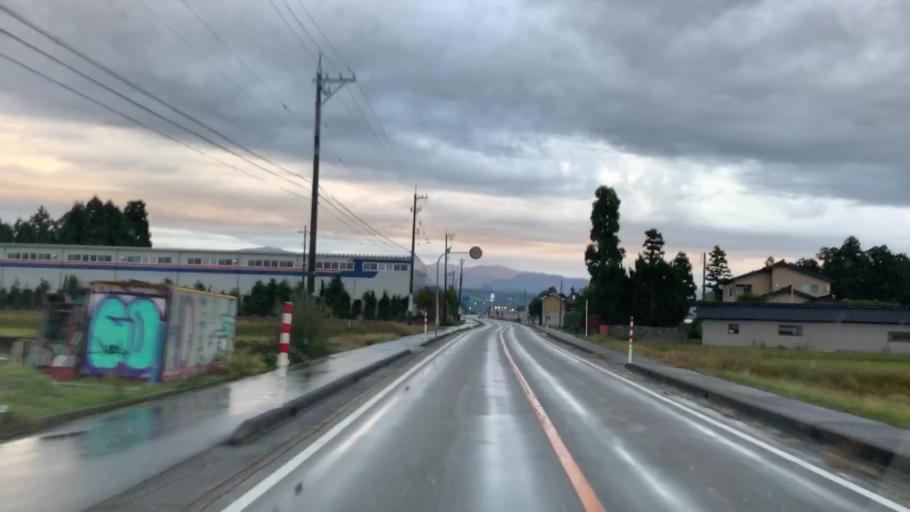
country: JP
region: Toyama
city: Kamiichi
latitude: 36.6561
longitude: 137.3281
